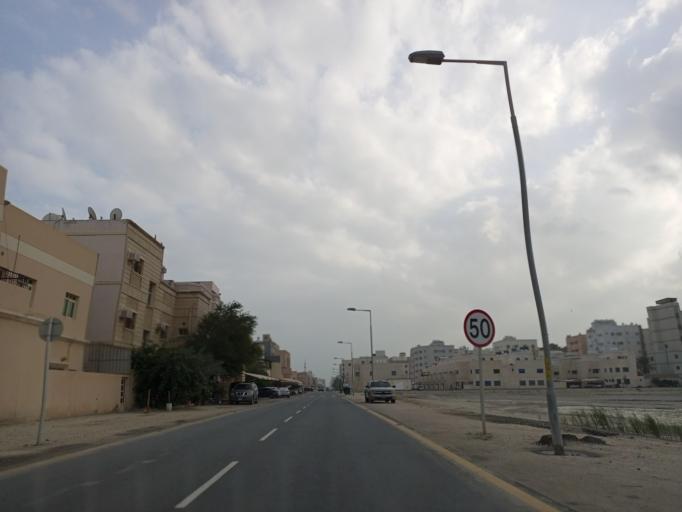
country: BH
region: Muharraq
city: Al Hadd
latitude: 26.2434
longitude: 50.6480
